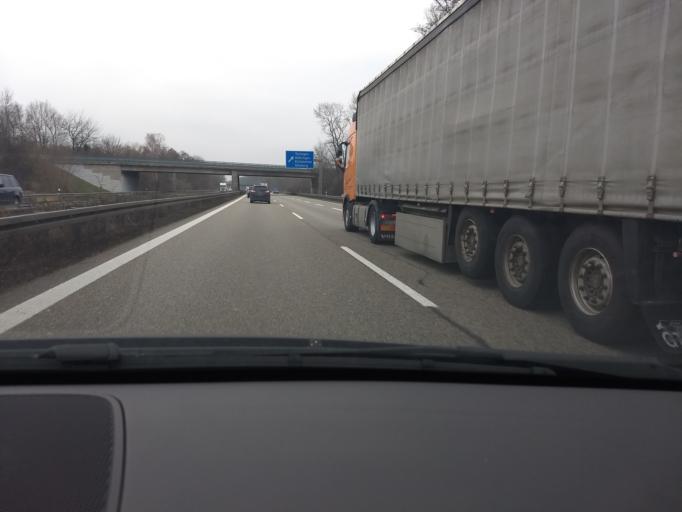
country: DE
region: Baden-Wuerttemberg
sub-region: Freiburg Region
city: Teningen
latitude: 48.1141
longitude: 7.7882
